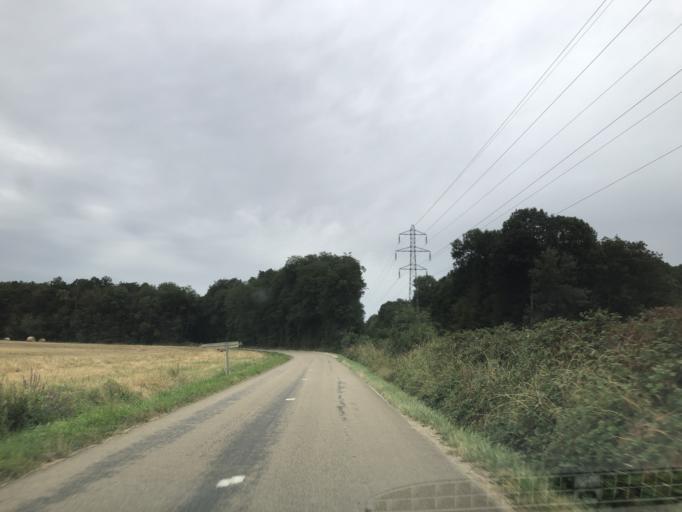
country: FR
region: Centre
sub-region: Departement du Loiret
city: Courtenay
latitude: 47.9958
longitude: 3.1439
